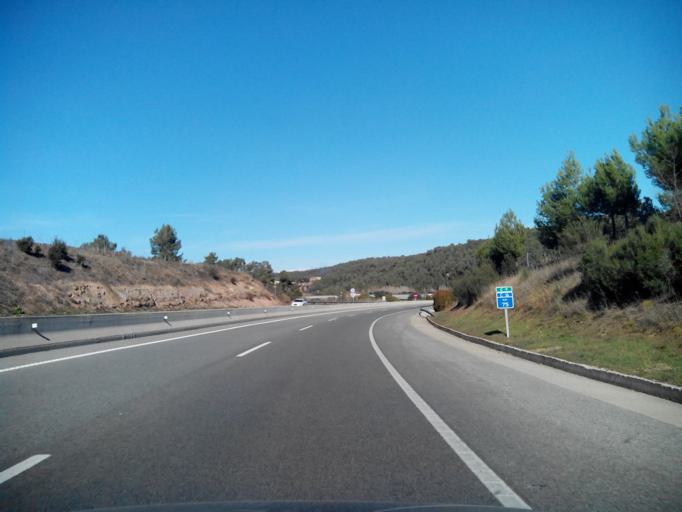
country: ES
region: Catalonia
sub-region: Provincia de Barcelona
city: Navas
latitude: 41.9148
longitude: 1.8819
